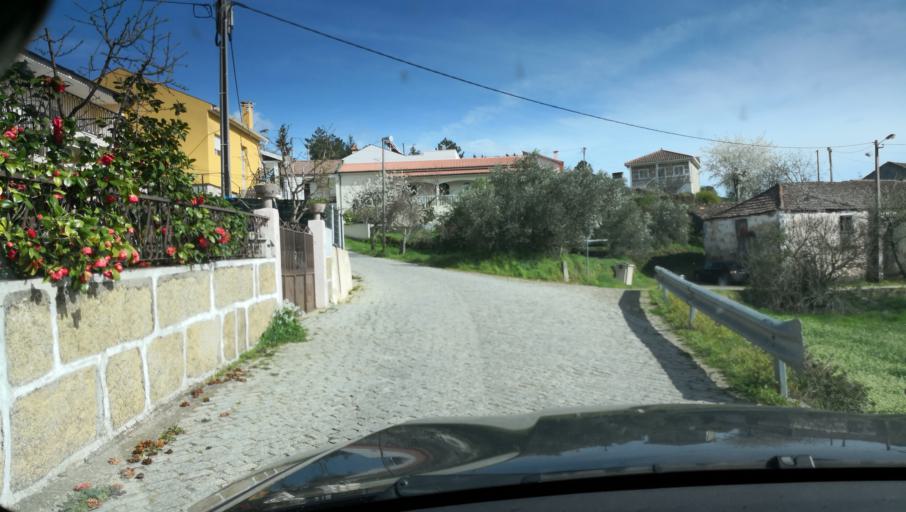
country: PT
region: Vila Real
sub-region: Sabrosa
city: Vilela
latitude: 41.2527
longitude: -7.6633
